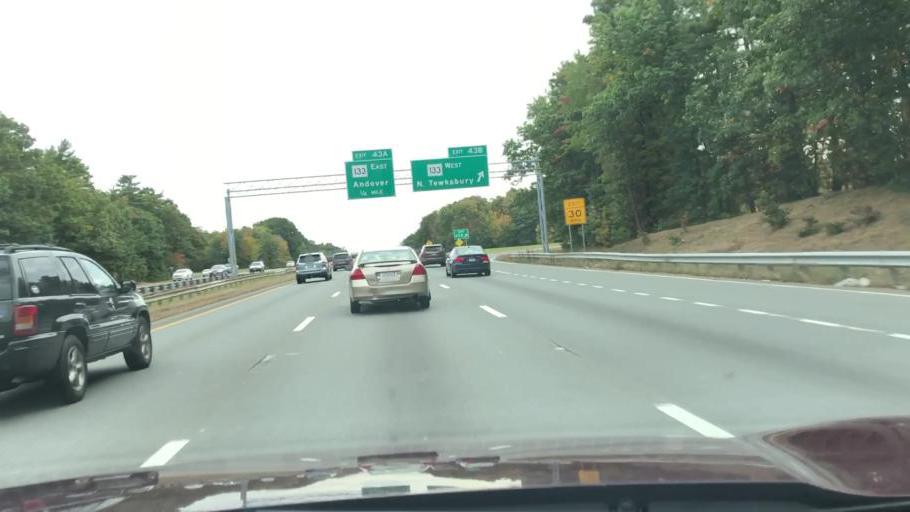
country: US
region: Massachusetts
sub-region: Essex County
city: Andover
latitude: 42.6499
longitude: -71.1879
